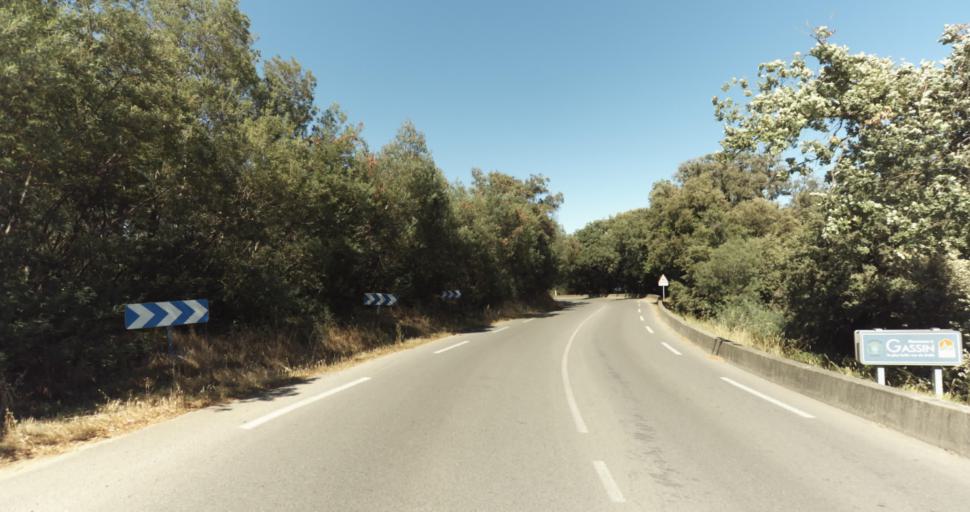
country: FR
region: Provence-Alpes-Cote d'Azur
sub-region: Departement du Var
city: La Croix-Valmer
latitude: 43.2157
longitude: 6.5686
